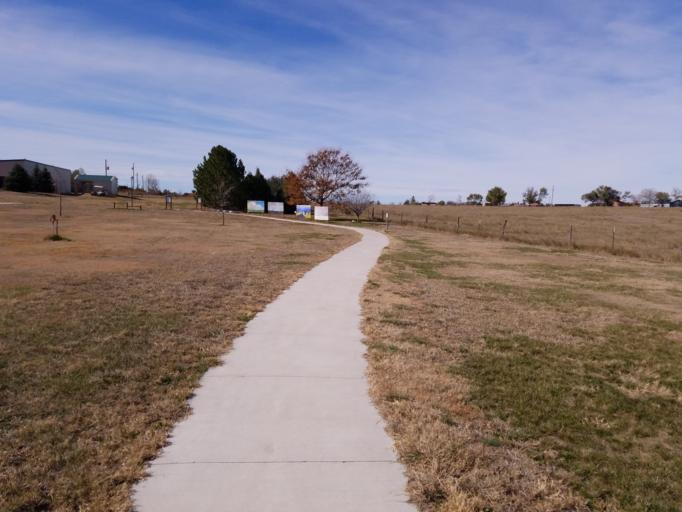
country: US
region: Colorado
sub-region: Yuma County
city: Yuma
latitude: 39.6571
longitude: -102.6741
